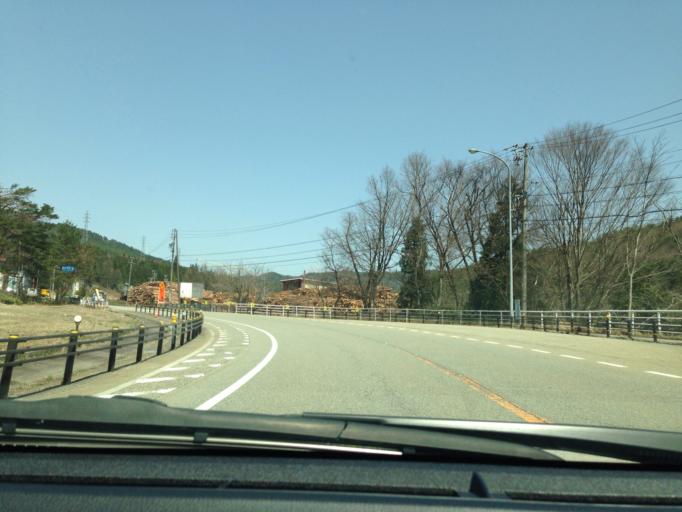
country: JP
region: Gifu
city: Takayama
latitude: 36.0635
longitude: 137.2691
